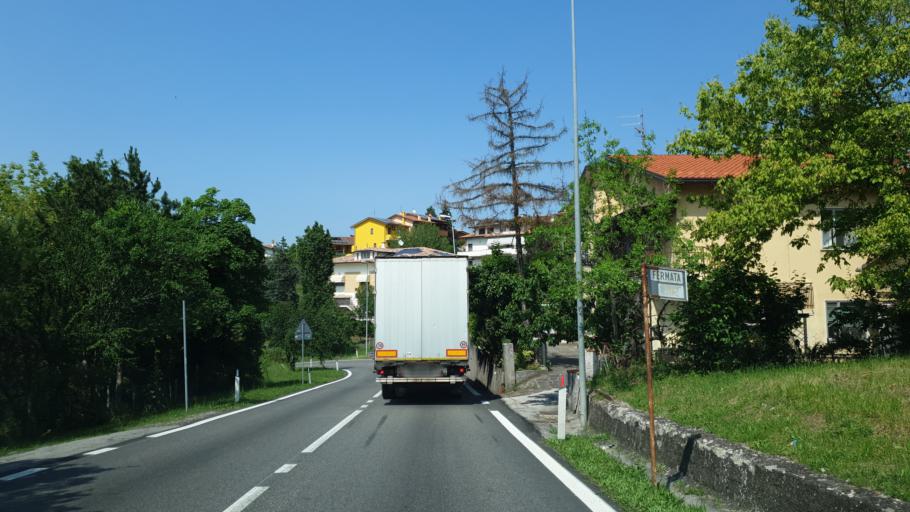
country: SM
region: Acquaviva
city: Acquaviva
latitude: 43.9459
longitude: 12.4185
